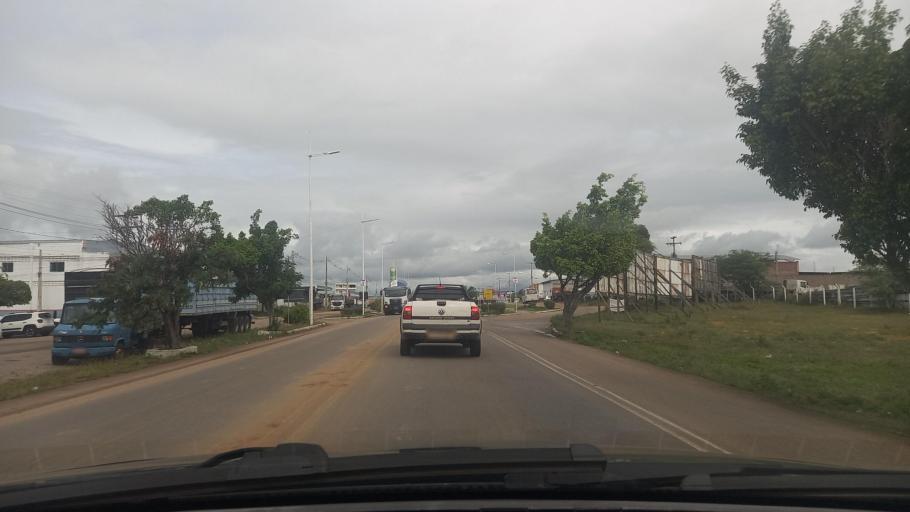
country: BR
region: Bahia
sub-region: Paulo Afonso
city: Paulo Afonso
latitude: -9.4373
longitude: -38.2253
